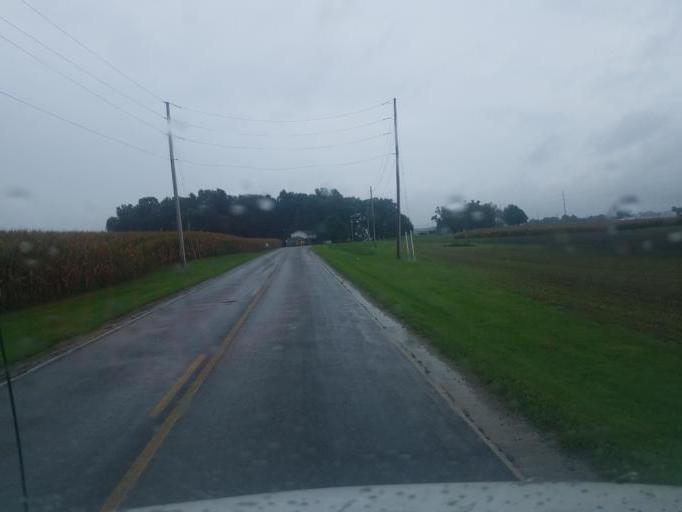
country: US
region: Ohio
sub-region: Medina County
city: Seville
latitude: 40.9965
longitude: -81.8566
